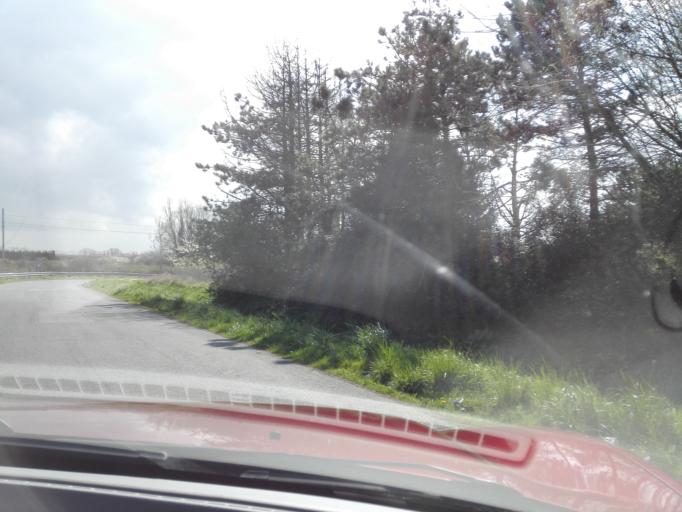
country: FR
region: Nord-Pas-de-Calais
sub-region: Departement du Nord
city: Grande-Synthe
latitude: 51.0030
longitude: 2.3056
